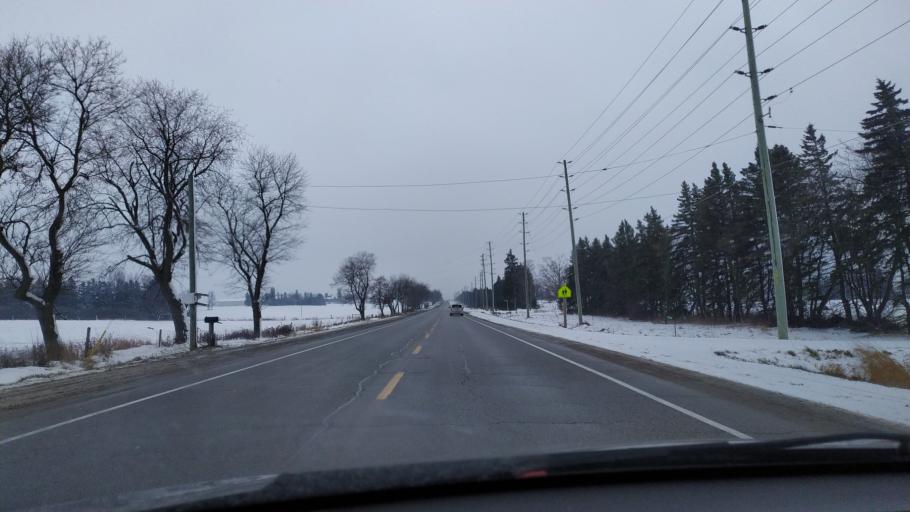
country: CA
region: Ontario
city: Waterloo
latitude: 43.6166
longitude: -80.6768
